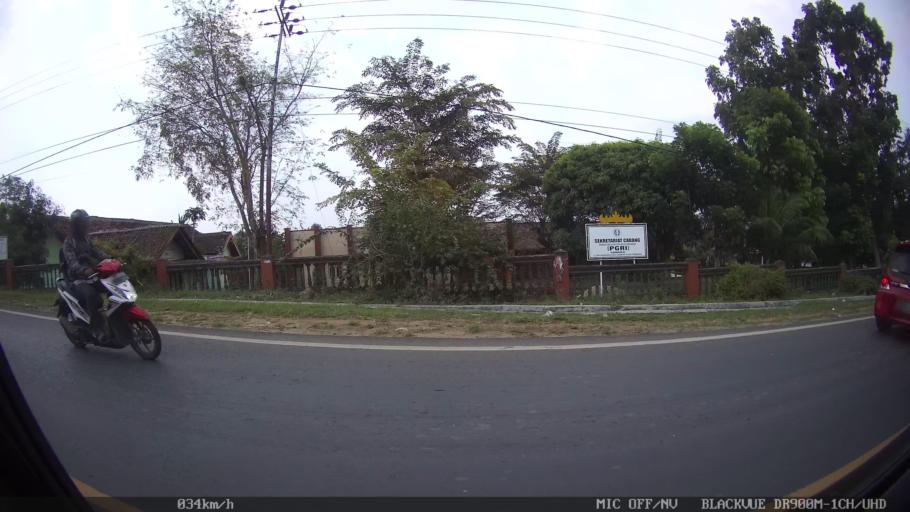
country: ID
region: Lampung
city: Gadingrejo
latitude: -5.3750
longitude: 105.0657
